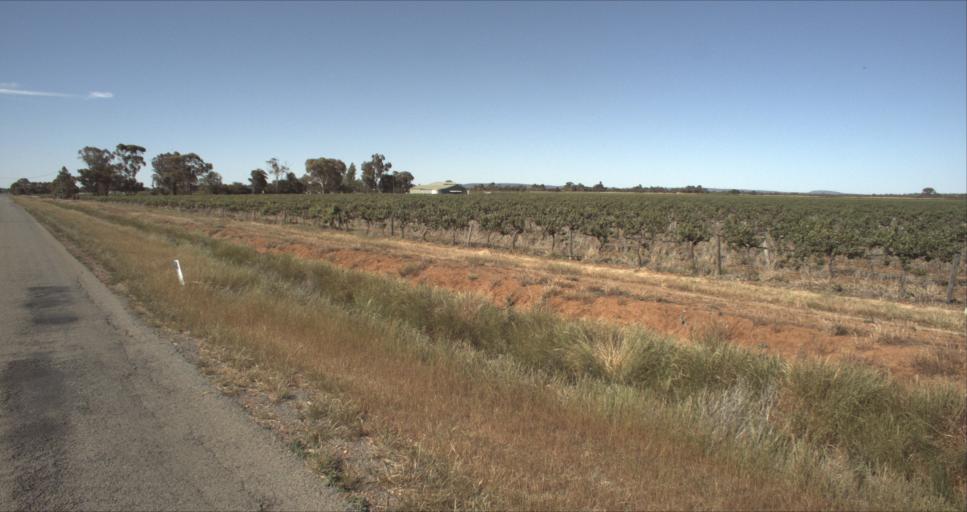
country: AU
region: New South Wales
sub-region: Leeton
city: Leeton
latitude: -34.5754
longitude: 146.3809
